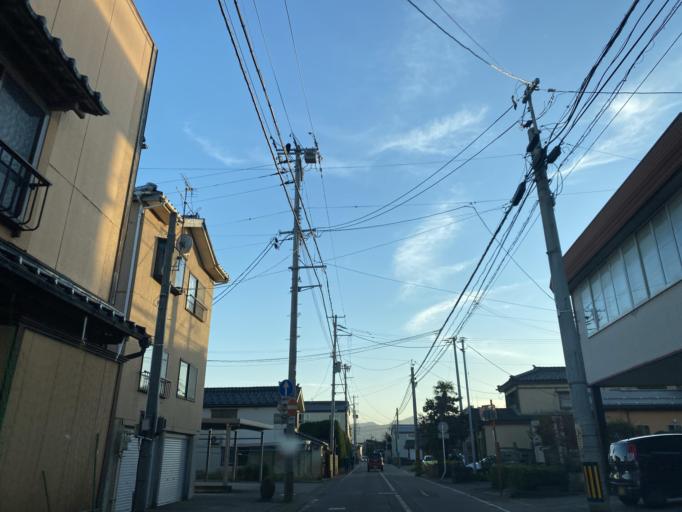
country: JP
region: Niigata
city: Kashiwazaki
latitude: 37.3775
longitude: 138.5655
